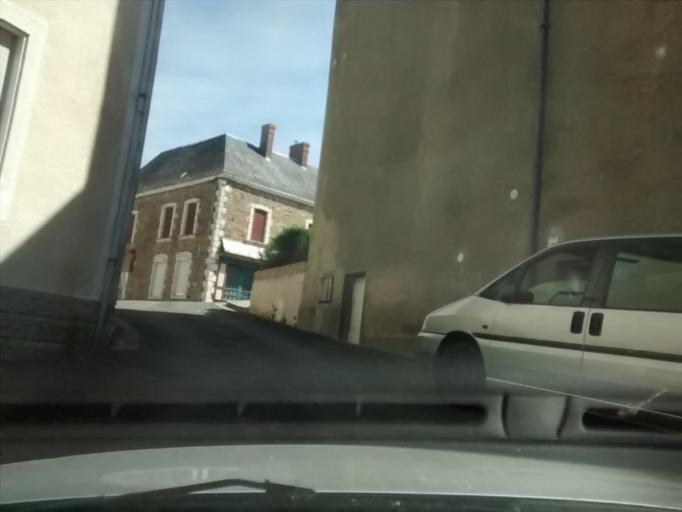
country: FR
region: Pays de la Loire
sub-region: Departement de la Sarthe
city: Brulon
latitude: 48.0274
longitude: -0.2735
